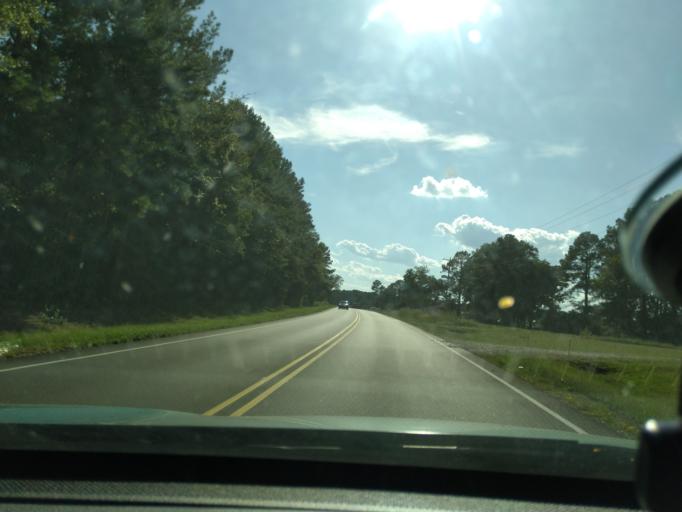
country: US
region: North Carolina
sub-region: Nash County
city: Sharpsburg
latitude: 35.9084
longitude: -77.8430
